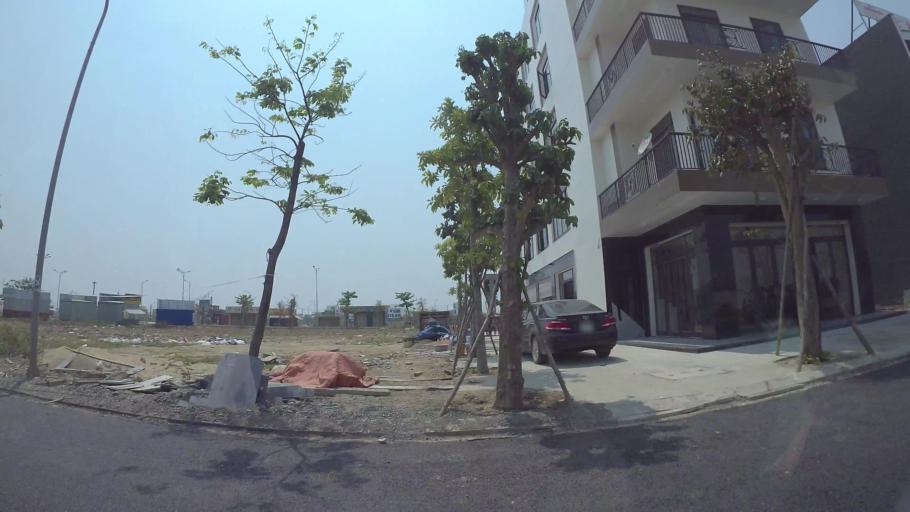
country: VN
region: Da Nang
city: Ngu Hanh Son
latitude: 16.0106
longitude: 108.2424
